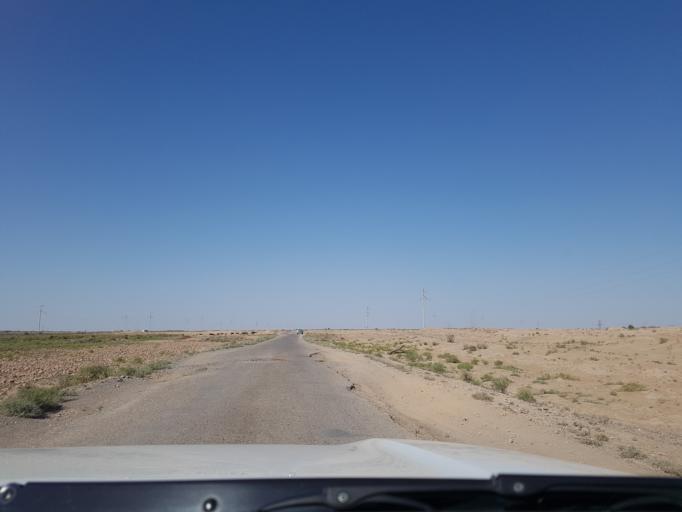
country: IR
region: Razavi Khorasan
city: Sarakhs
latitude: 36.5278
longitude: 61.2424
